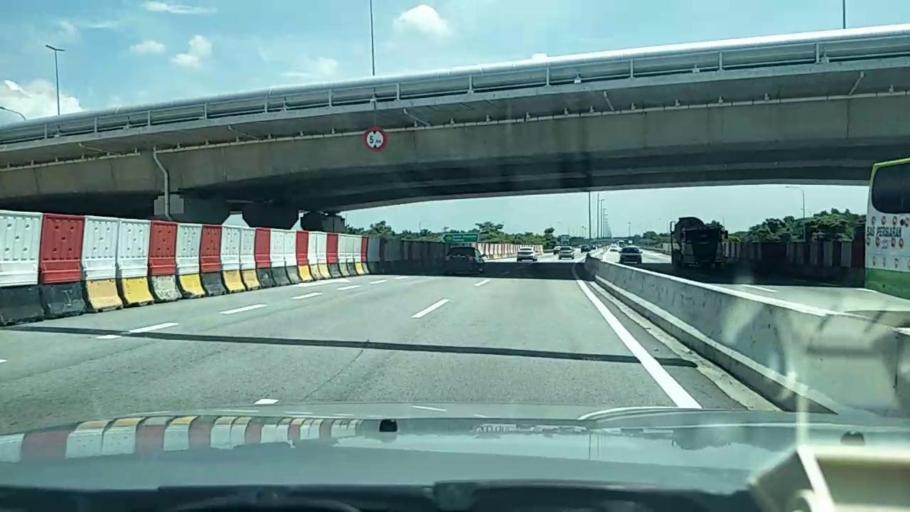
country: MY
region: Putrajaya
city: Putrajaya
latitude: 2.9287
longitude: 101.6231
